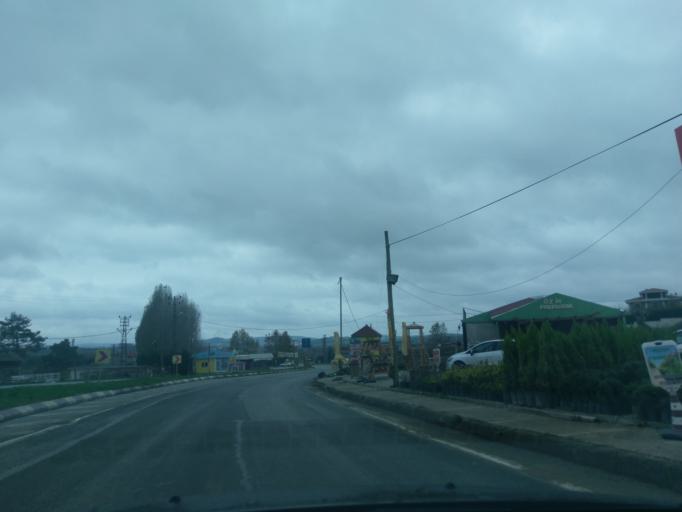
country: TR
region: Istanbul
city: Catalca
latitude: 41.1596
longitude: 28.4544
